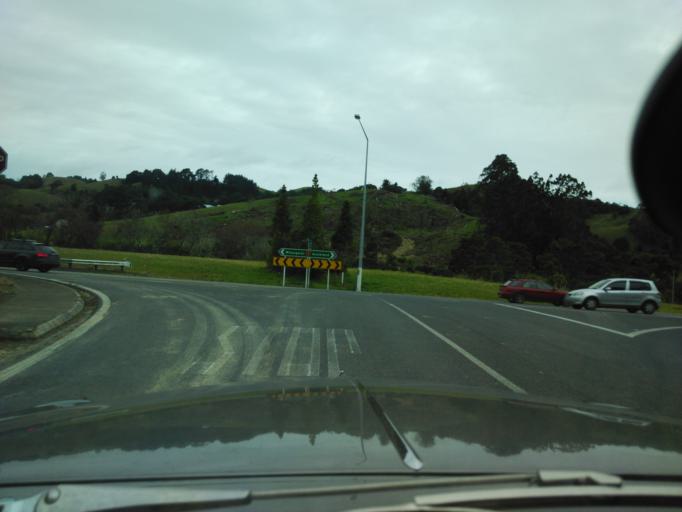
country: NZ
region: Auckland
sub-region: Auckland
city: Warkworth
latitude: -36.5164
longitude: 174.6690
